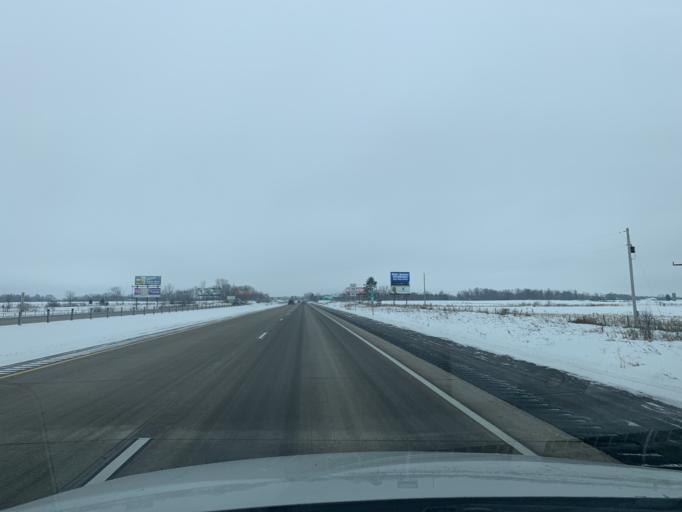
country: US
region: Minnesota
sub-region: Pine County
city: Rock Creek
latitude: 45.7577
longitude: -92.9909
